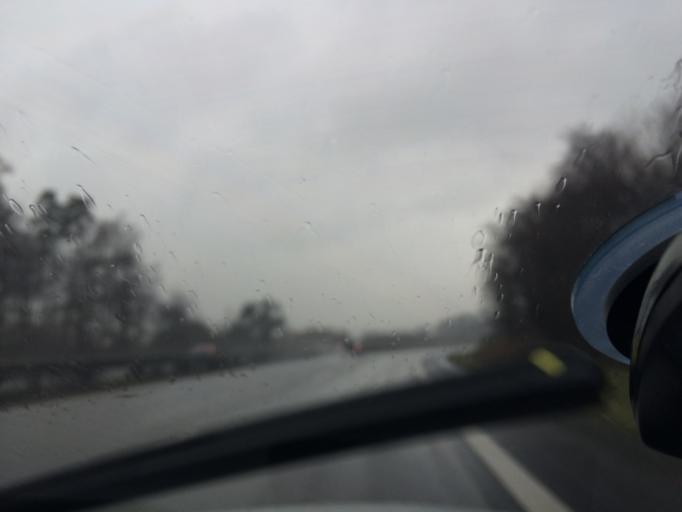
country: DE
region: Hesse
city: Staufenberg
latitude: 50.6856
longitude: 8.7215
